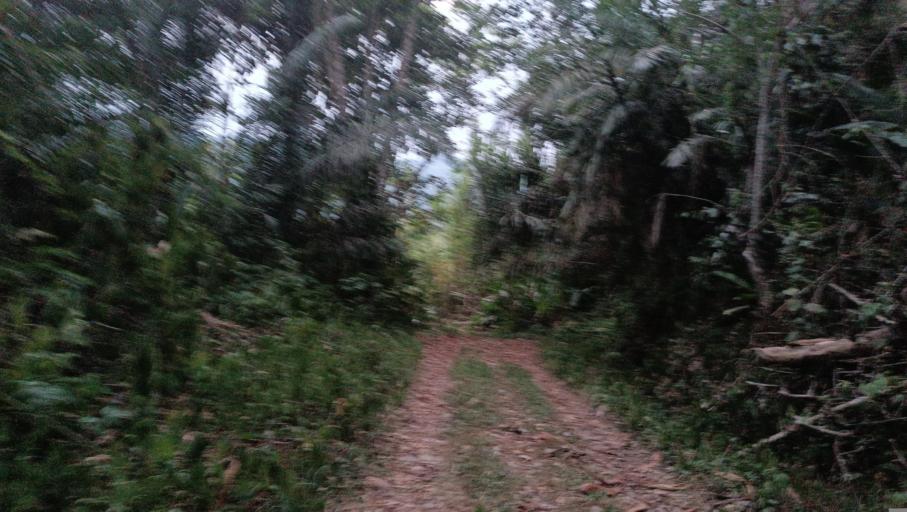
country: BO
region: La Paz
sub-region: Provincia Larecaja
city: Guanay
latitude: -15.5682
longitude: -67.3266
